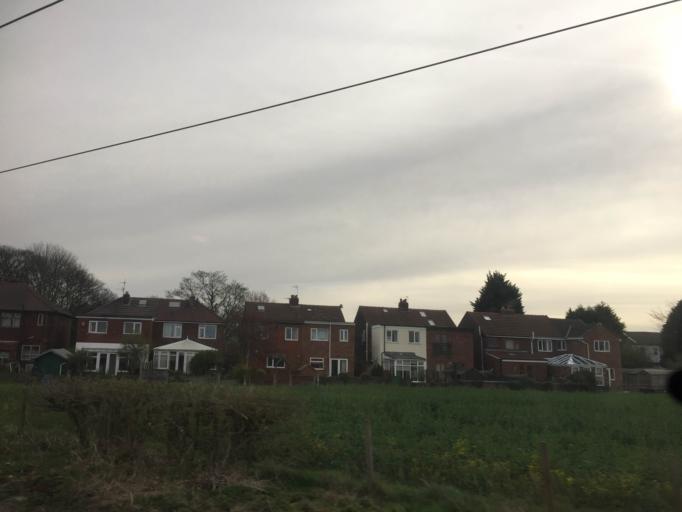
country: GB
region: England
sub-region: St. Helens
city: Newton-le-Willows
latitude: 53.4591
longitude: -2.6018
